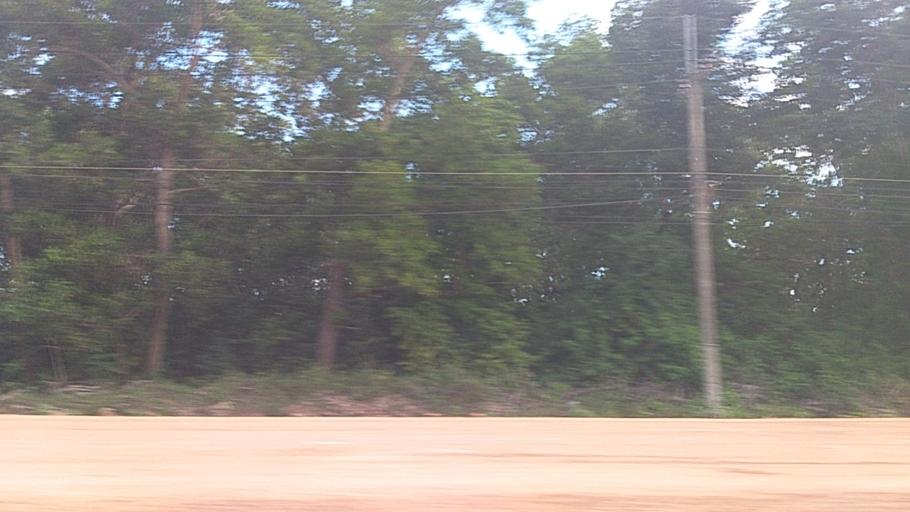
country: TH
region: Surin
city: Kap Choeng
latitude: 14.4629
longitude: 103.6492
